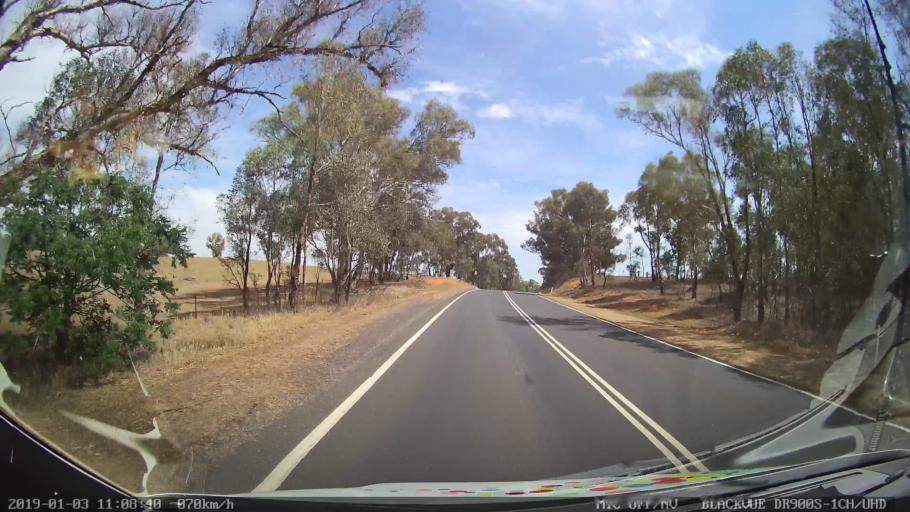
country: AU
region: New South Wales
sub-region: Young
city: Young
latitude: -34.2470
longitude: 148.2562
